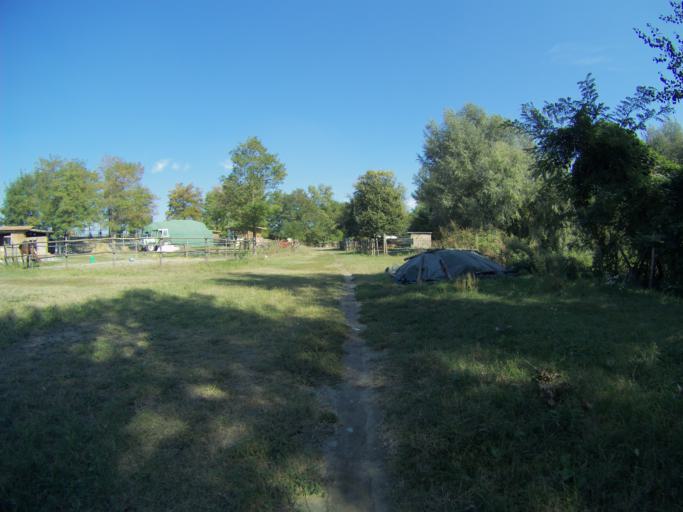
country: IT
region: Emilia-Romagna
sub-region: Provincia di Reggio Emilia
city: Forche
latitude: 44.6452
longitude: 10.5895
